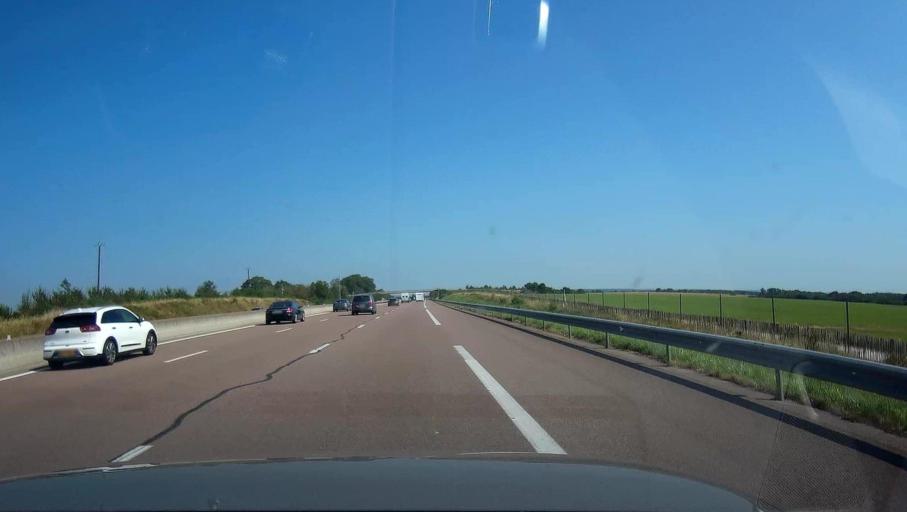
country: FR
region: Bourgogne
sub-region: Departement de la Cote-d'Or
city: Selongey
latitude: 47.7163
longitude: 5.1897
